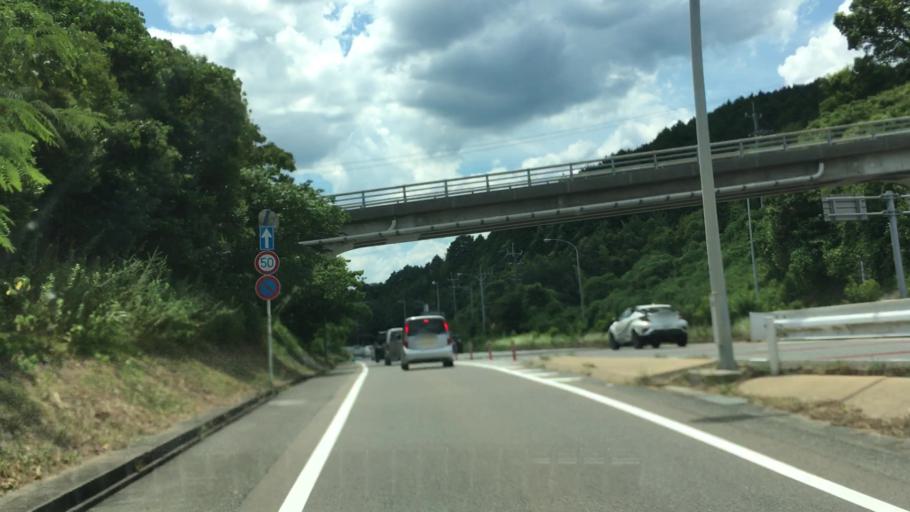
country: JP
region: Fukuoka
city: Chikushino-shi
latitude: 33.4421
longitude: 130.5281
